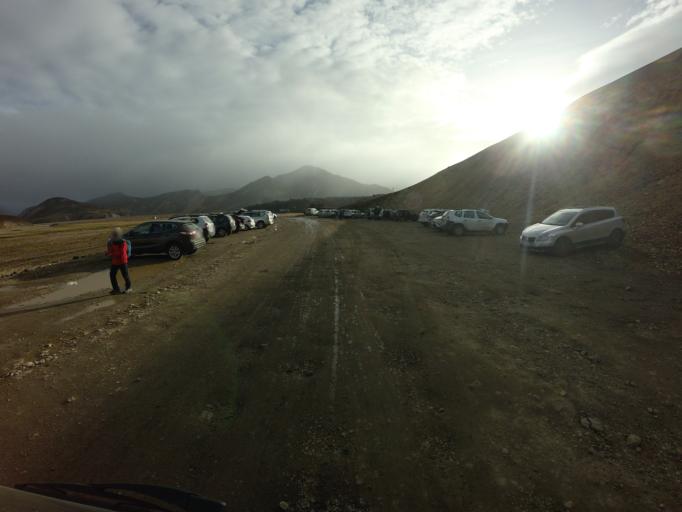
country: IS
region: South
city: Vestmannaeyjar
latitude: 63.9951
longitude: -19.0596
